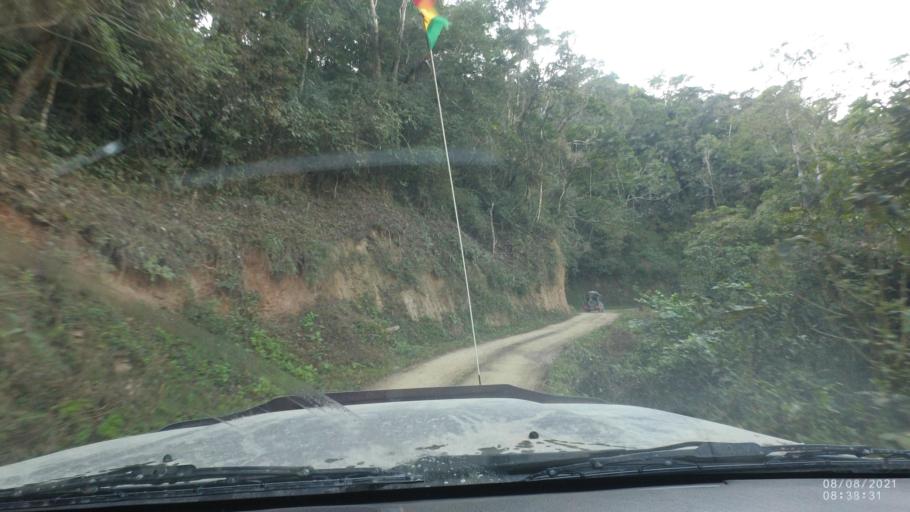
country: BO
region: La Paz
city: Quime
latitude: -16.5257
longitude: -66.7669
